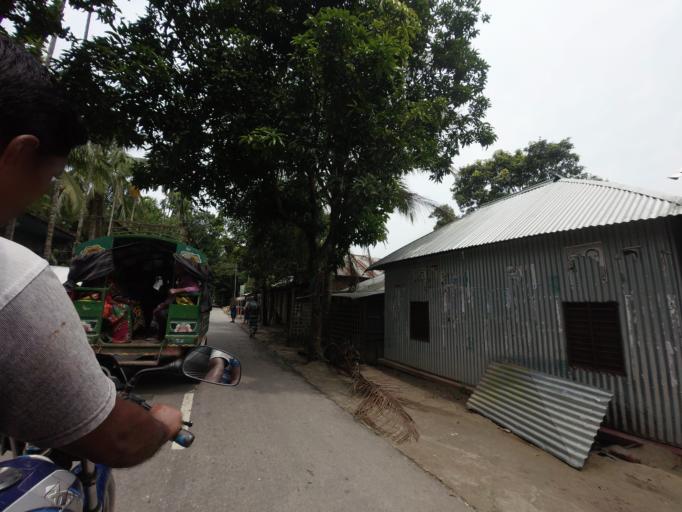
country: BD
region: Khulna
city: Kalia
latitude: 23.0865
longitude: 89.6662
